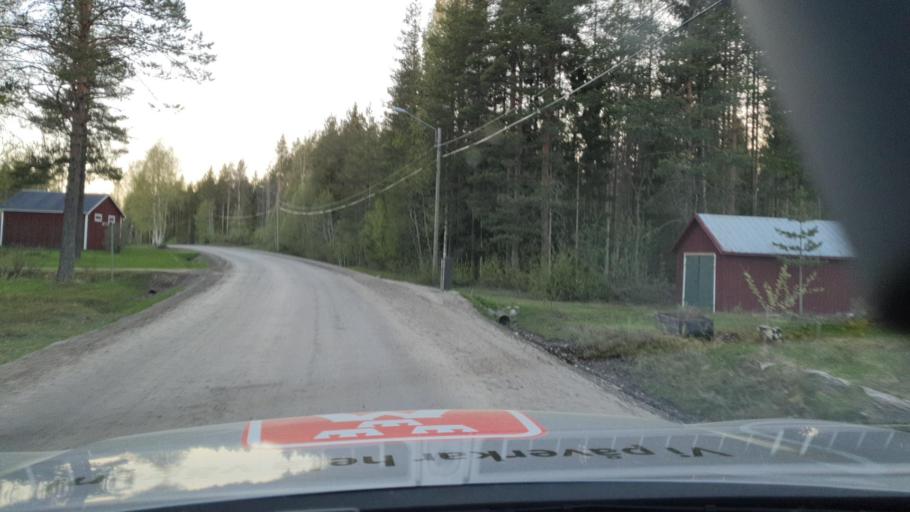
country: SE
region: Vaesternorrland
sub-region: OErnskoeldsviks Kommun
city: Ornskoldsvik
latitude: 63.5286
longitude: 18.5745
